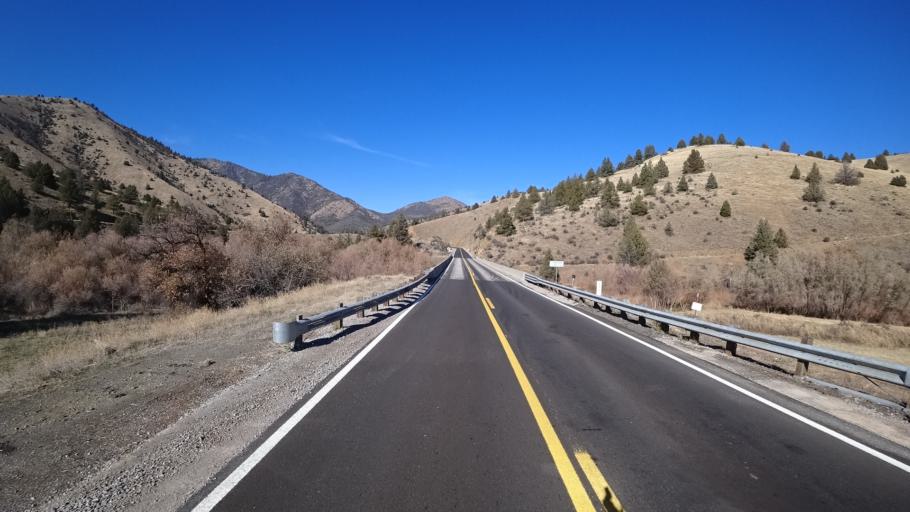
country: US
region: California
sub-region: Siskiyou County
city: Yreka
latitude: 41.7808
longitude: -122.5964
